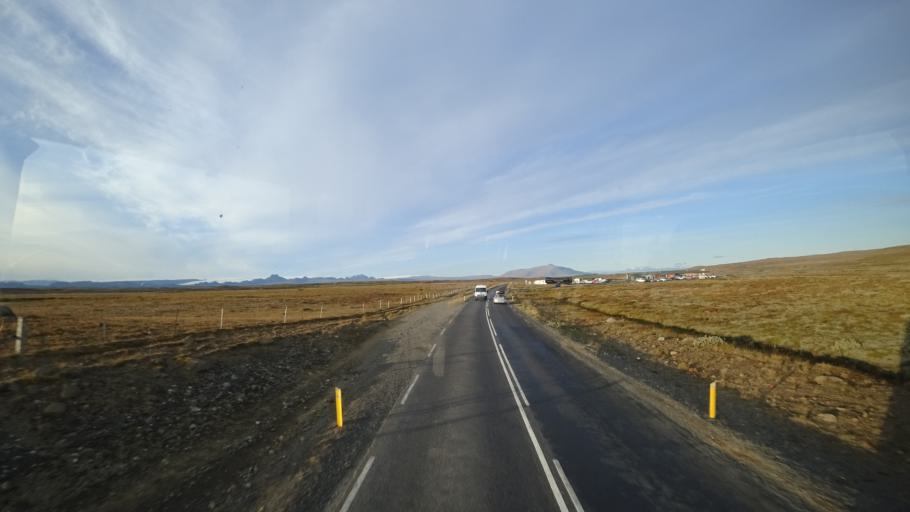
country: IS
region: South
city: Vestmannaeyjar
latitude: 64.3239
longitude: -20.1337
